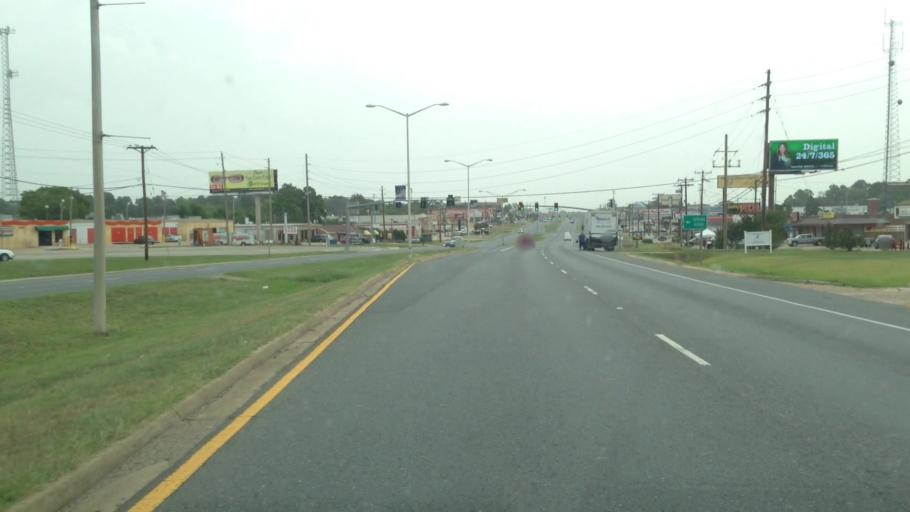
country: US
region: Louisiana
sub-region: De Soto Parish
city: Stonewall
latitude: 32.3949
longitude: -93.8111
